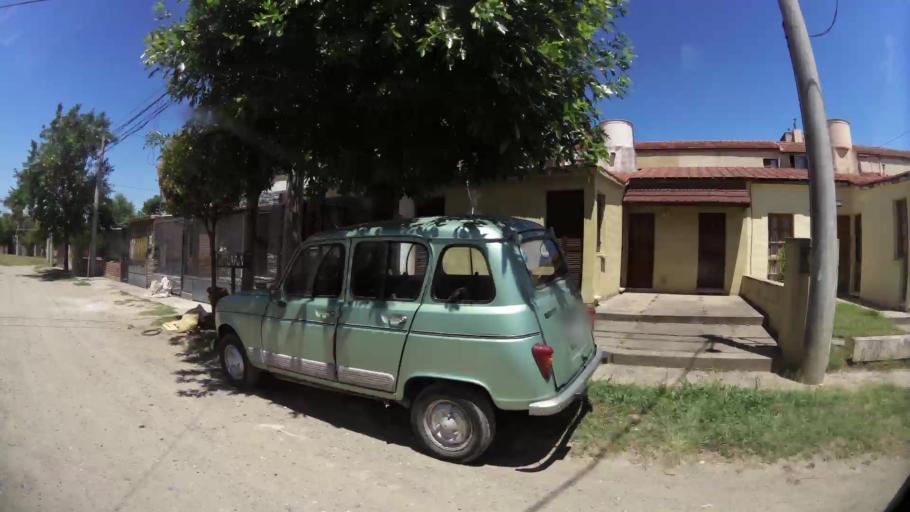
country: AR
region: Cordoba
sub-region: Departamento de Capital
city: Cordoba
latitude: -31.3857
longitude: -64.1407
